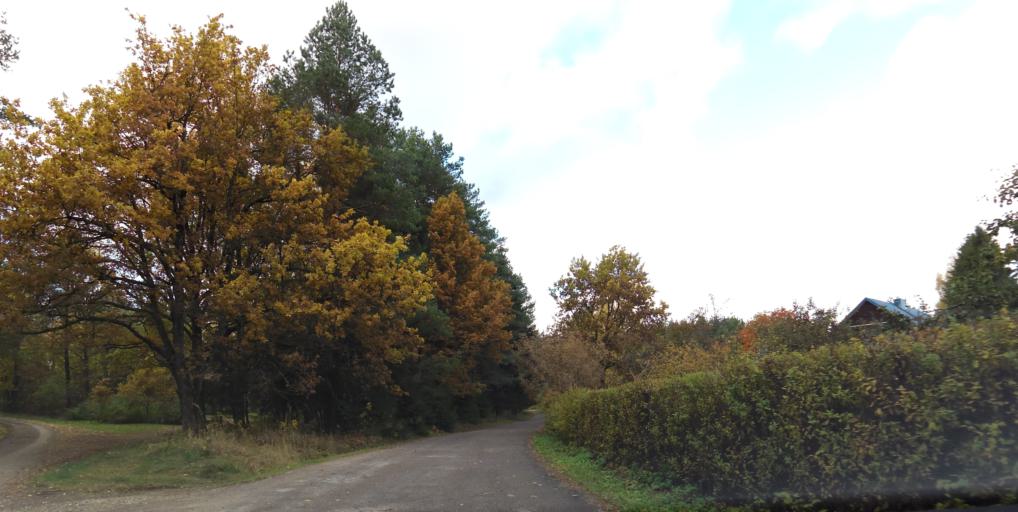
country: LT
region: Vilnius County
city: Vilkpede
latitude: 54.6478
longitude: 25.2548
